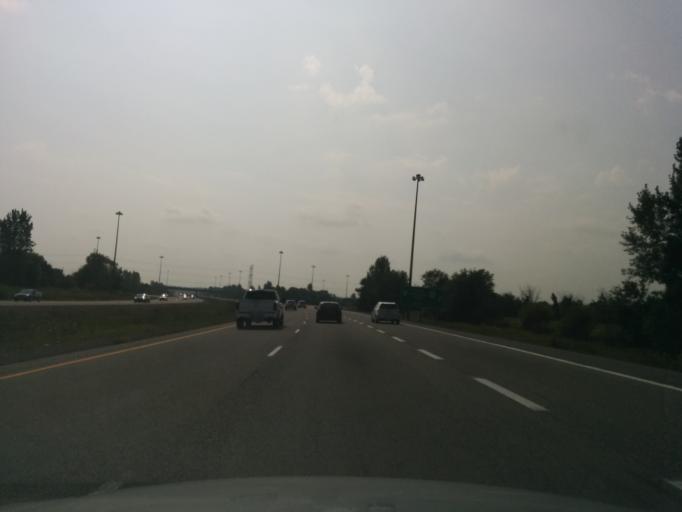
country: CA
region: Ontario
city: Bells Corners
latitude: 45.3179
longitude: -75.8057
